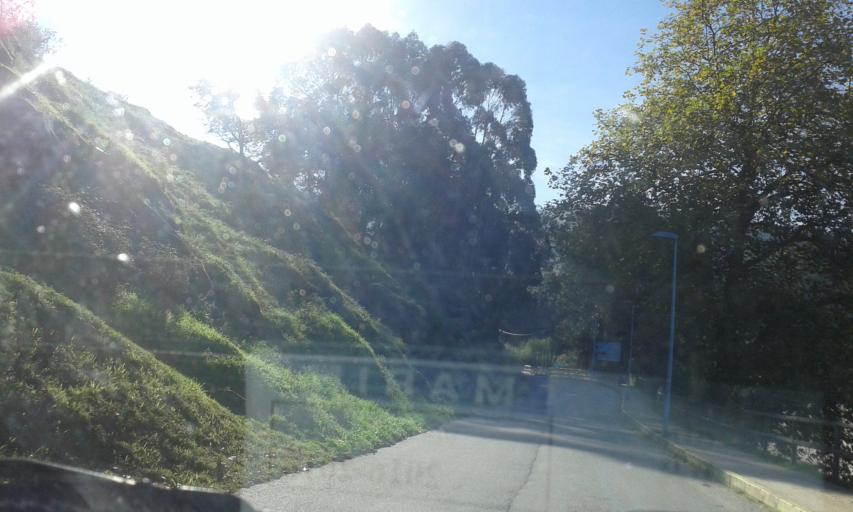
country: ES
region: Galicia
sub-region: Provincia de Pontevedra
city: Marin
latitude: 42.3873
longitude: -8.7196
